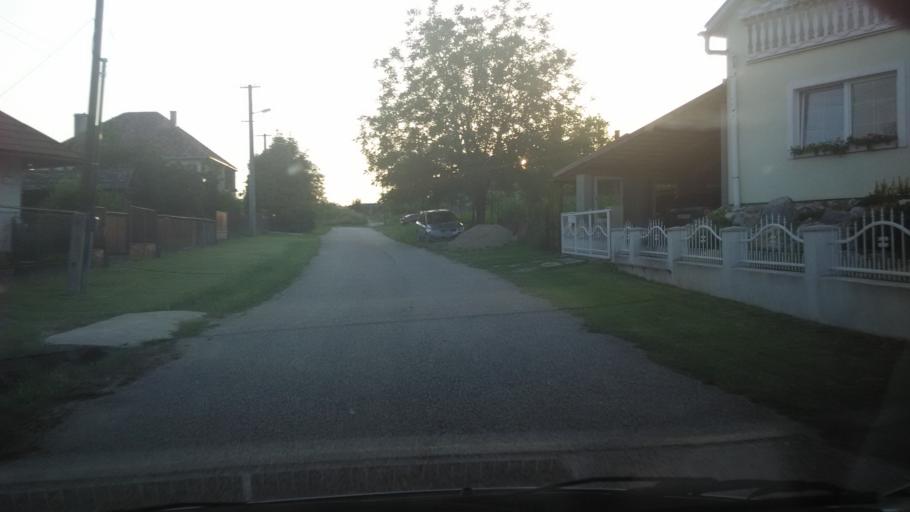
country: SK
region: Nitriansky
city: Levice
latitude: 48.1338
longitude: 18.4599
